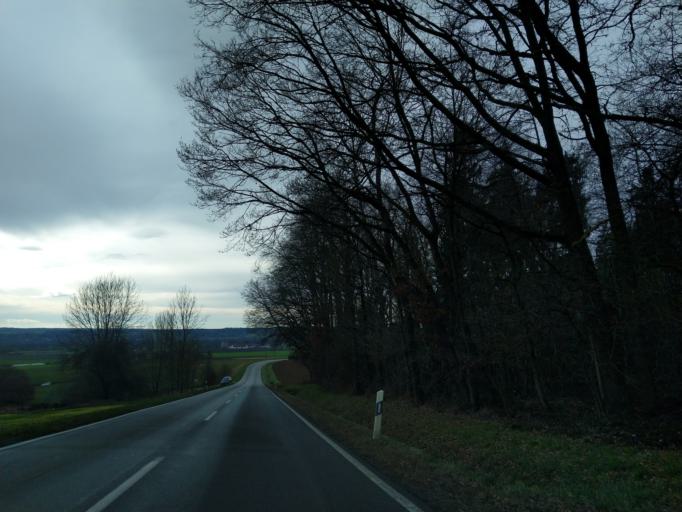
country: DE
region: Bavaria
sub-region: Lower Bavaria
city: Aldersbach
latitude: 48.6292
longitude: 13.0223
